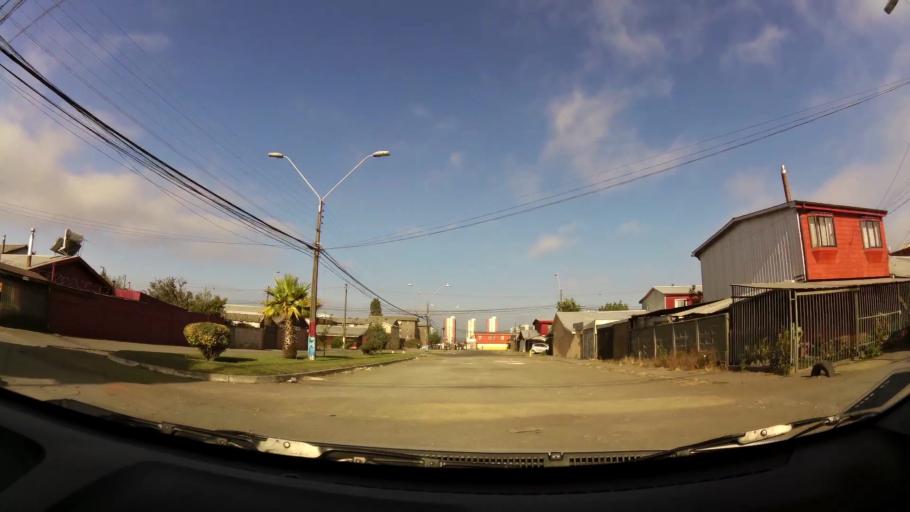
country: CL
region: Biobio
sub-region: Provincia de Concepcion
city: Concepcion
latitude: -36.7880
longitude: -73.0980
